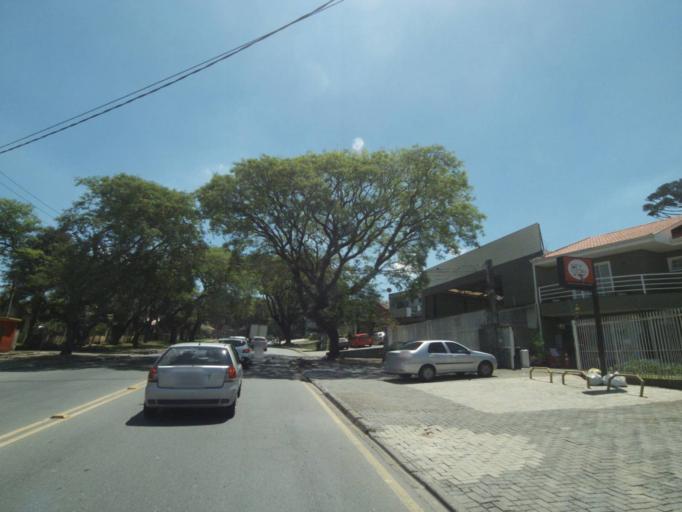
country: BR
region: Parana
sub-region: Pinhais
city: Pinhais
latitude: -25.3897
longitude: -49.2230
